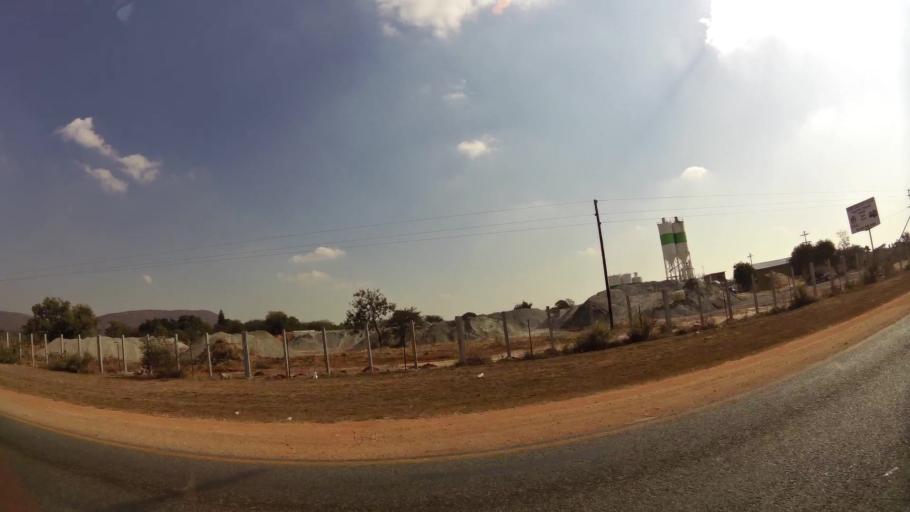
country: ZA
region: North-West
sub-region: Bojanala Platinum District Municipality
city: Mogwase
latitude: -25.4748
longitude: 27.0869
